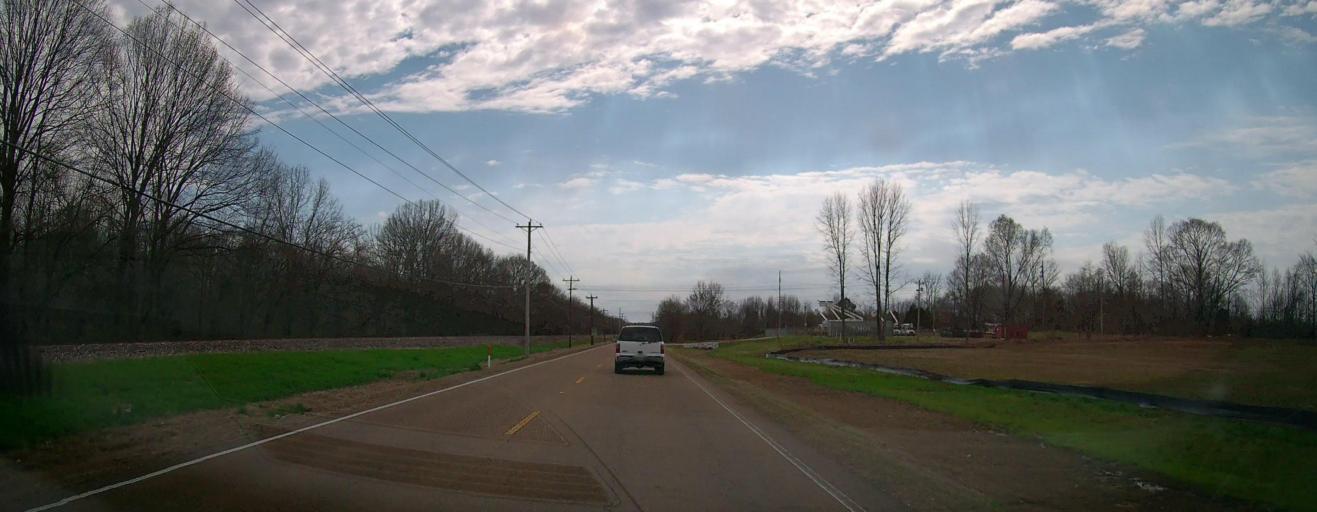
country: US
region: Mississippi
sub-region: De Soto County
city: Olive Branch
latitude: 34.9135
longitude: -89.7625
